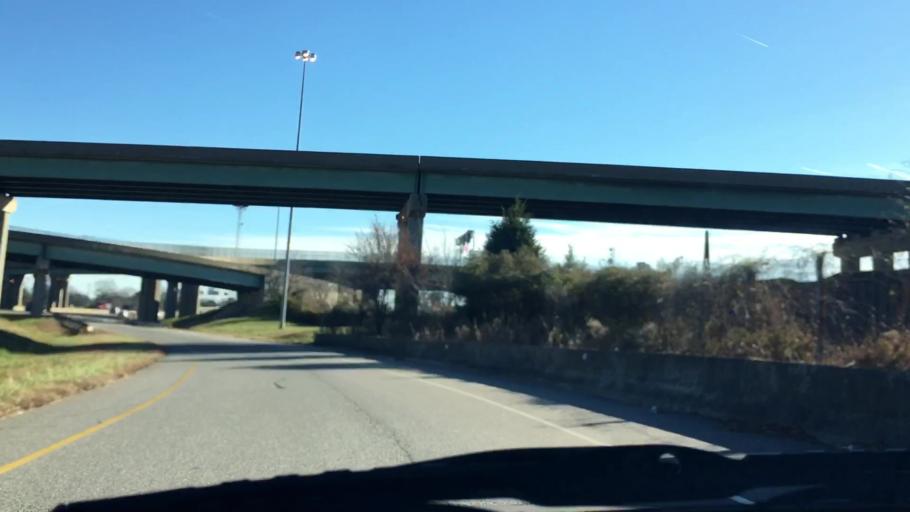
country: US
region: Virginia
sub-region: City of Newport News
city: Newport News
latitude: 36.9809
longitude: -76.4252
